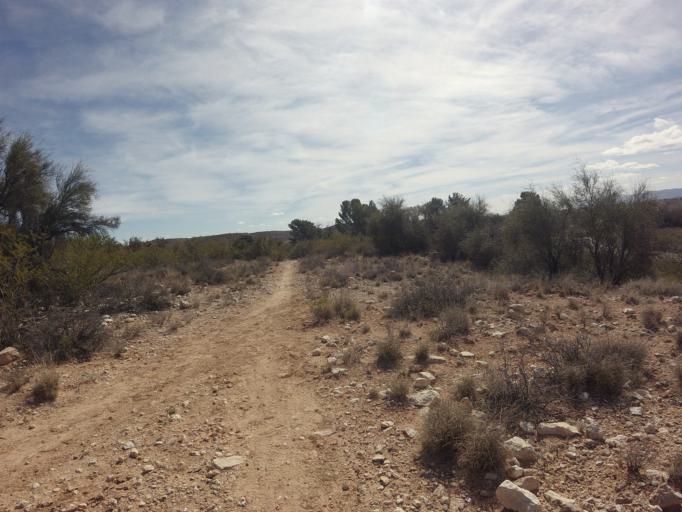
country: US
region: Arizona
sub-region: Yavapai County
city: Cottonwood
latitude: 34.7551
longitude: -112.0143
